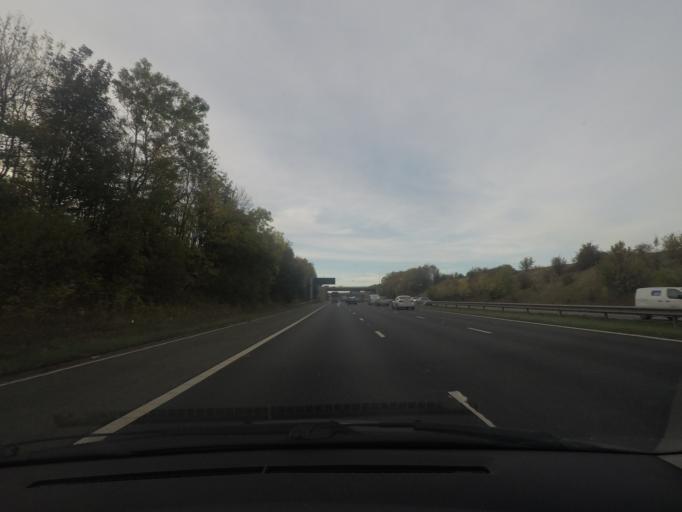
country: GB
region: England
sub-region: Barnsley
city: Dodworth
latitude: 53.5461
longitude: -1.5138
